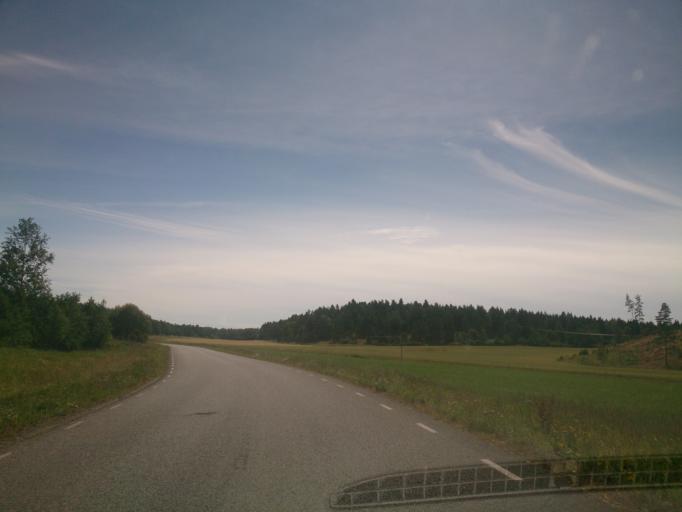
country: SE
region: OEstergoetland
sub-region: Valdemarsviks Kommun
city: Valdemarsvik
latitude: 58.2853
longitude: 16.6754
